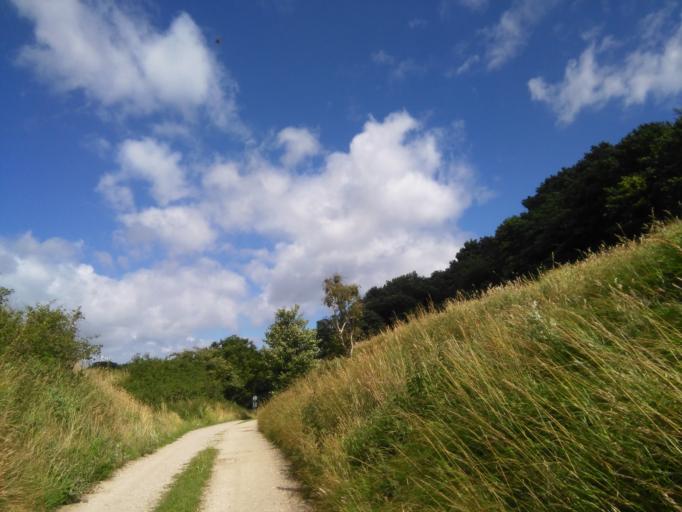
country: DK
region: Central Jutland
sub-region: Arhus Kommune
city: Logten
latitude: 56.1681
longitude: 10.4087
